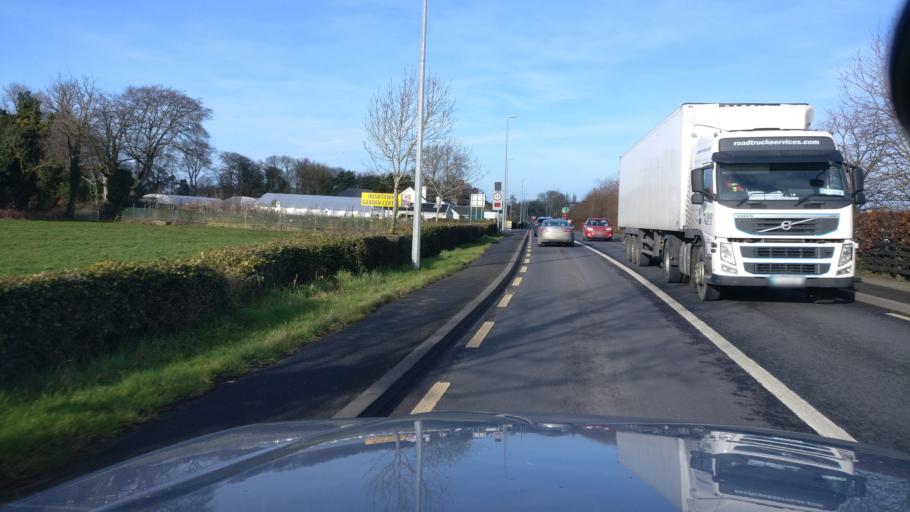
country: IE
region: Leinster
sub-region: Laois
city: Mountmellick
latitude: 53.1073
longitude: -7.3292
